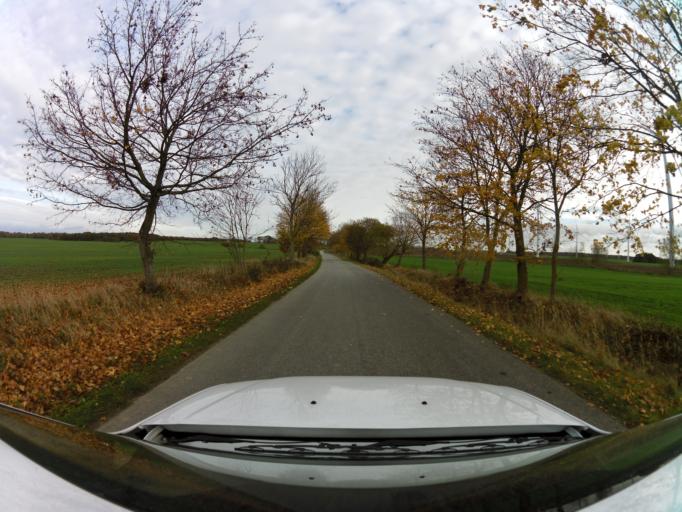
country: PL
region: West Pomeranian Voivodeship
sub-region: Powiat gryficki
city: Karnice
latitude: 54.0492
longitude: 15.0811
